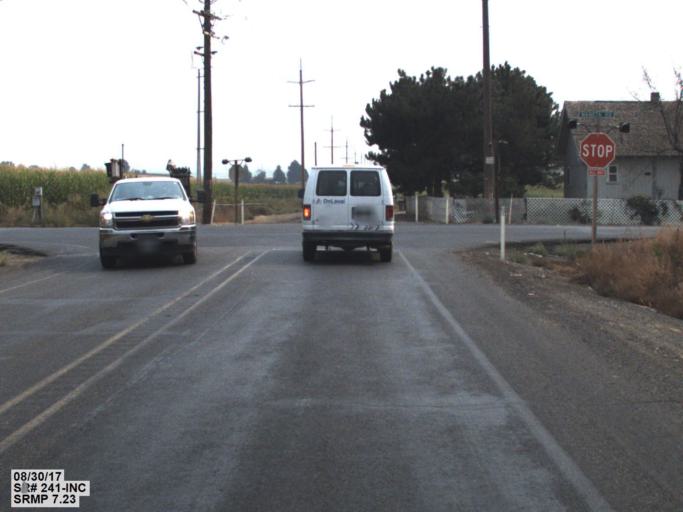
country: US
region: Washington
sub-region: Yakima County
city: Sunnyside
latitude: 46.3023
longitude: -119.9787
